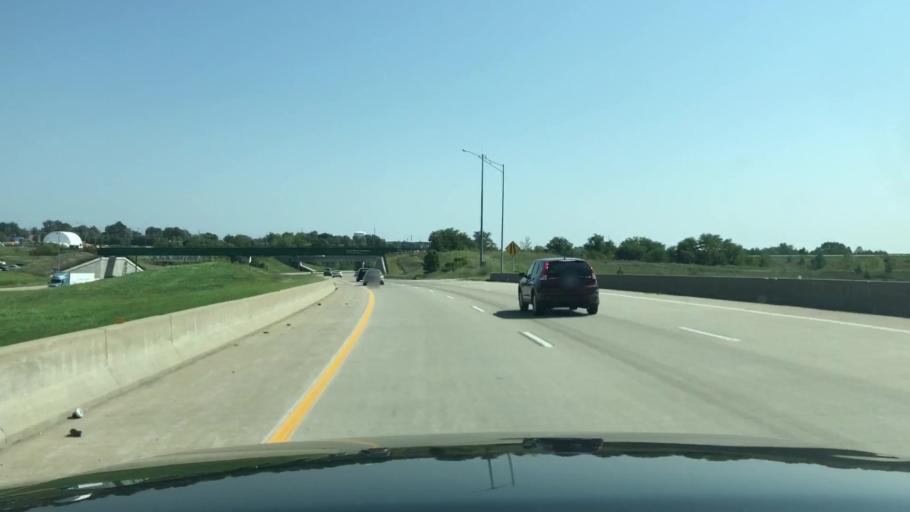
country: US
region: Missouri
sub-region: Saint Charles County
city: Saint Charles
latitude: 38.7542
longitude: -90.5471
